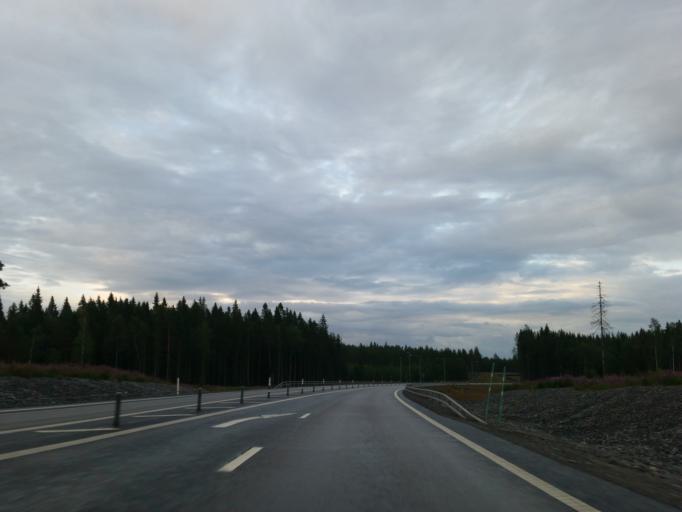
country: SE
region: Vaesterbotten
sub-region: Umea Kommun
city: Umea
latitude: 63.8542
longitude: 20.2765
